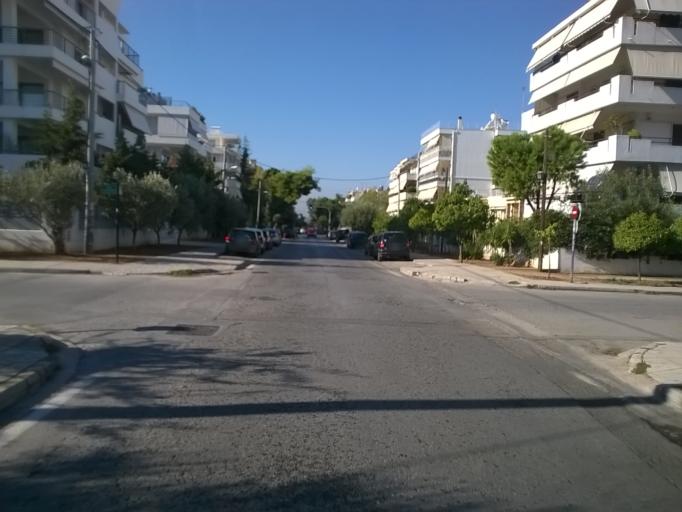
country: GR
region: Attica
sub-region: Nomarchia Athinas
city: Glyfada
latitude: 37.8658
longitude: 23.7515
